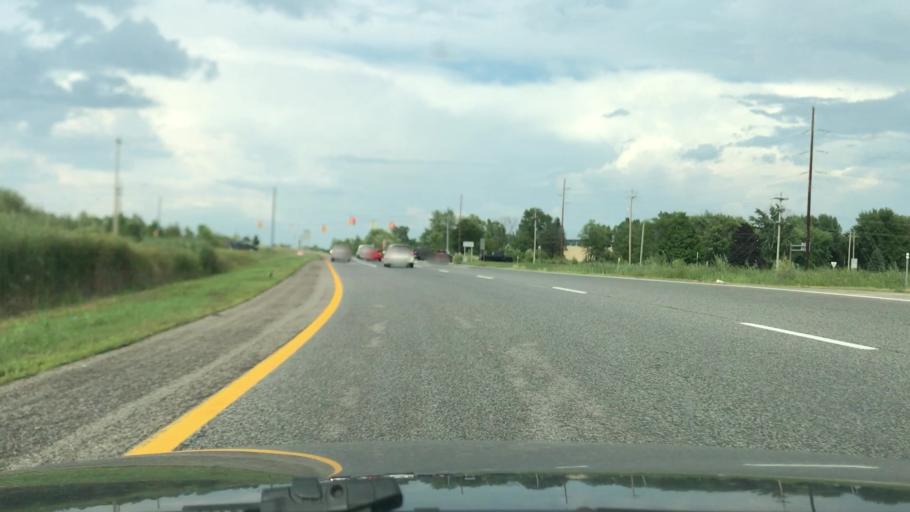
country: US
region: Michigan
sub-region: Kent County
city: Caledonia
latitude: 42.8488
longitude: -85.5395
